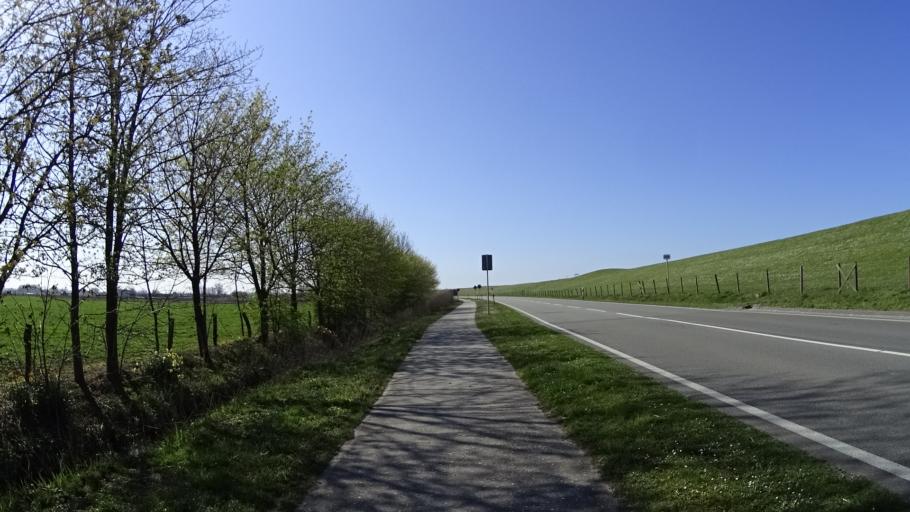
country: DE
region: Lower Saxony
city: Jemgum
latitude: 53.2610
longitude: 7.4065
